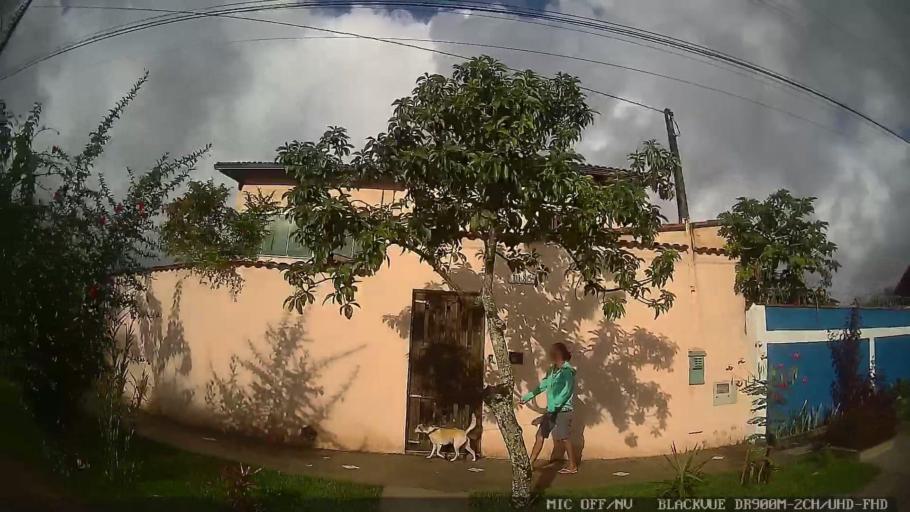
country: BR
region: Sao Paulo
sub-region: Itanhaem
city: Itanhaem
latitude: -24.1979
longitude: -46.8684
